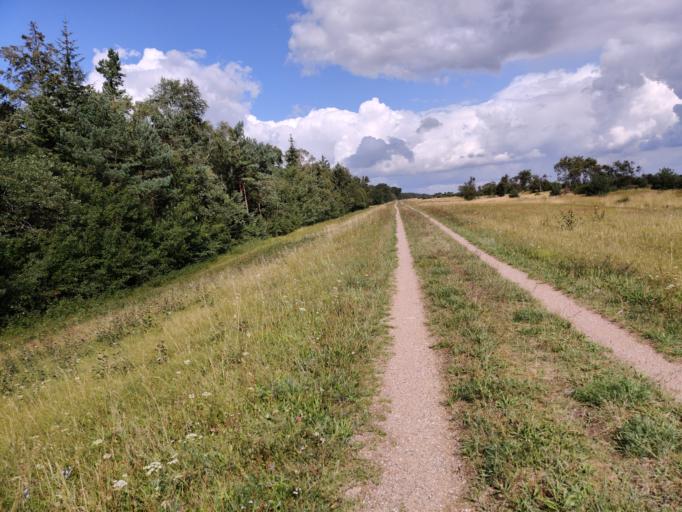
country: DK
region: Zealand
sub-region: Guldborgsund Kommune
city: Nykobing Falster
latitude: 54.6137
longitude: 11.9647
